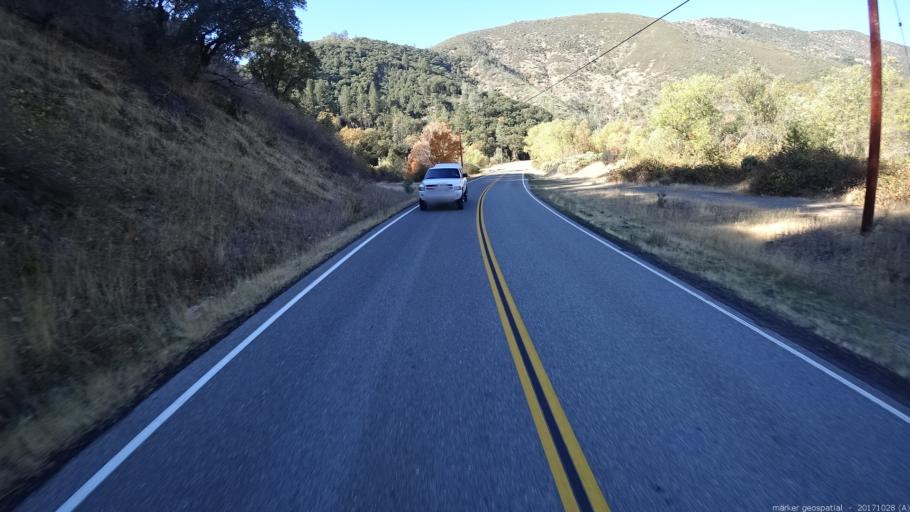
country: US
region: California
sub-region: Shasta County
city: Shasta
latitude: 40.6786
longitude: -122.6370
